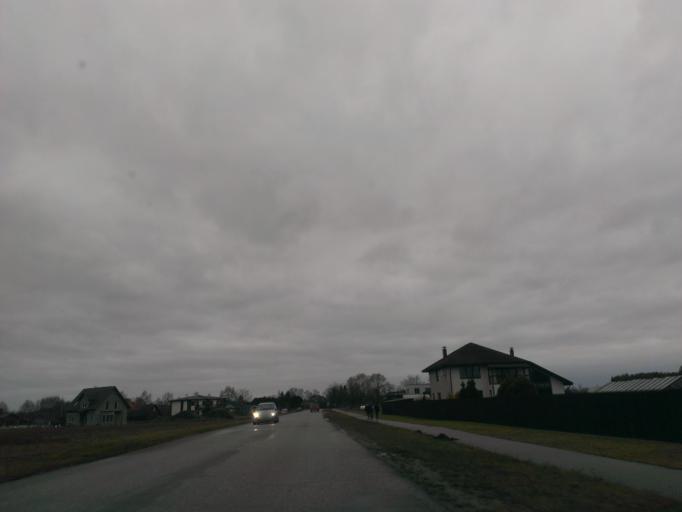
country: LV
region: Adazi
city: Adazi
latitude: 57.0699
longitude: 24.3422
